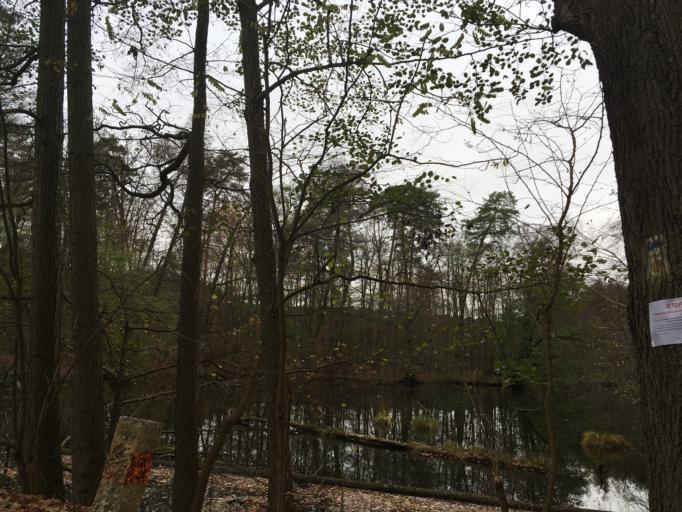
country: DE
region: Brandenburg
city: Mixdorf
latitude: 52.1633
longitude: 14.4403
